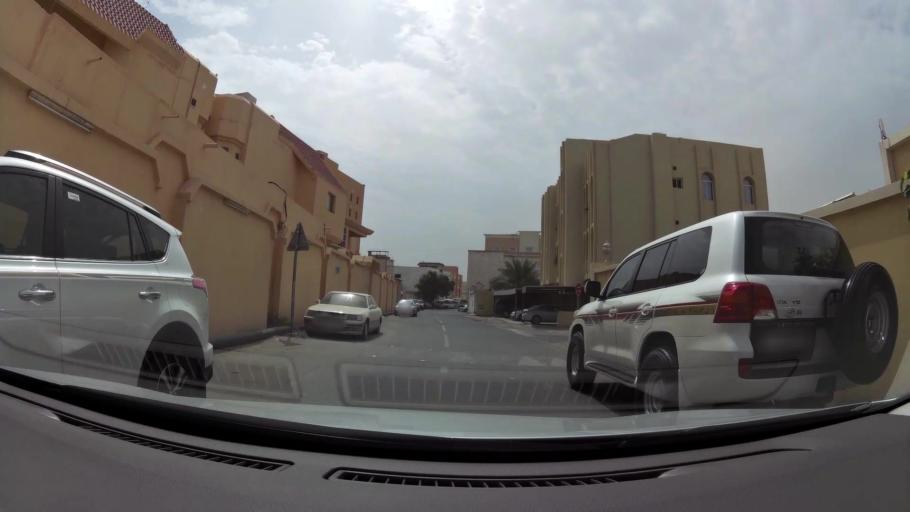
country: QA
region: Baladiyat ad Dawhah
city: Doha
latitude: 25.3049
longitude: 51.4981
